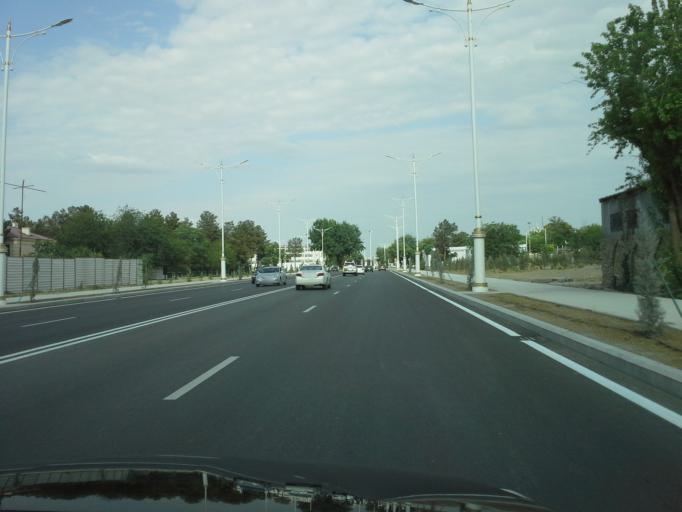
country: TM
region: Ahal
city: Ashgabat
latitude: 37.9582
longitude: 58.3427
